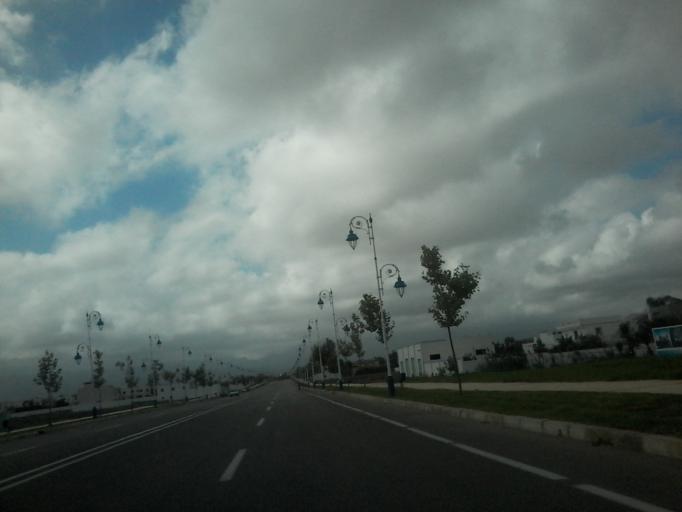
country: MA
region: Tanger-Tetouan
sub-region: Tetouan
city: Martil
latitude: 35.6536
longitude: -5.2947
